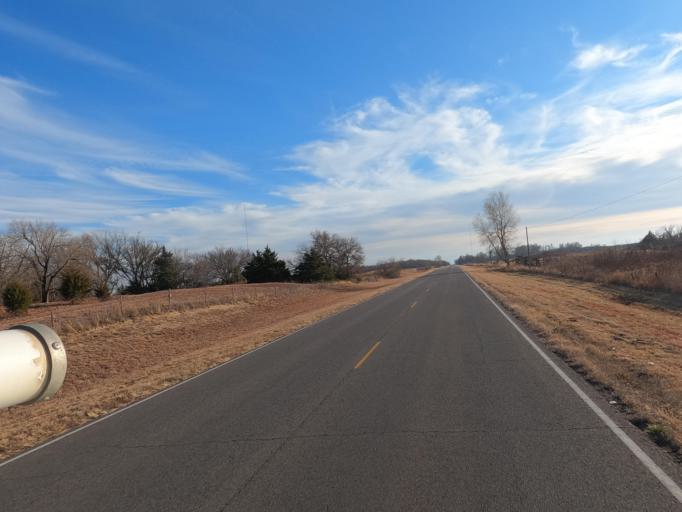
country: US
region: Kansas
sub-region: Reno County
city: Buhler
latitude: 38.0801
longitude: -97.7754
